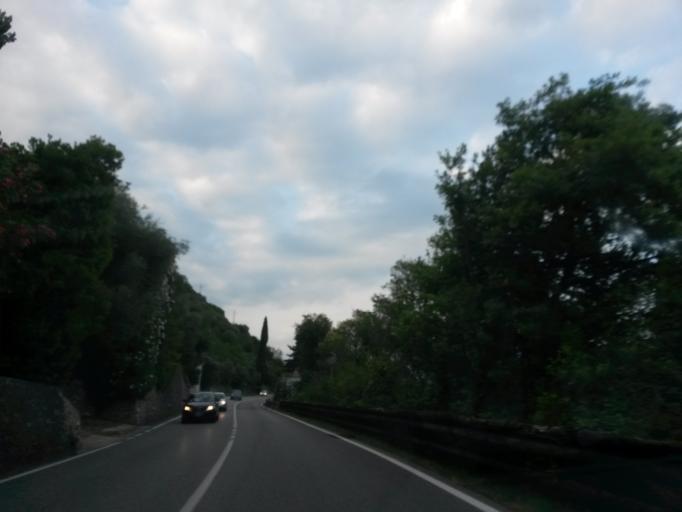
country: IT
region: Lombardy
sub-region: Provincia di Brescia
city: Toscolano Maderno
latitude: 45.6498
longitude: 10.6249
